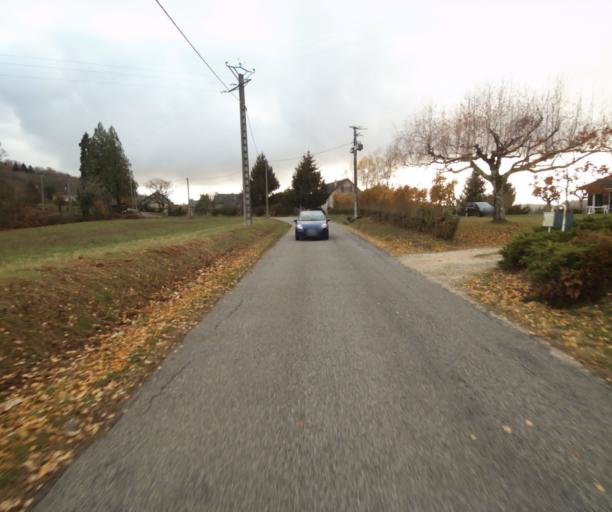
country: FR
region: Limousin
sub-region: Departement de la Correze
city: Sainte-Fortunade
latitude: 45.2088
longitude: 1.7787
